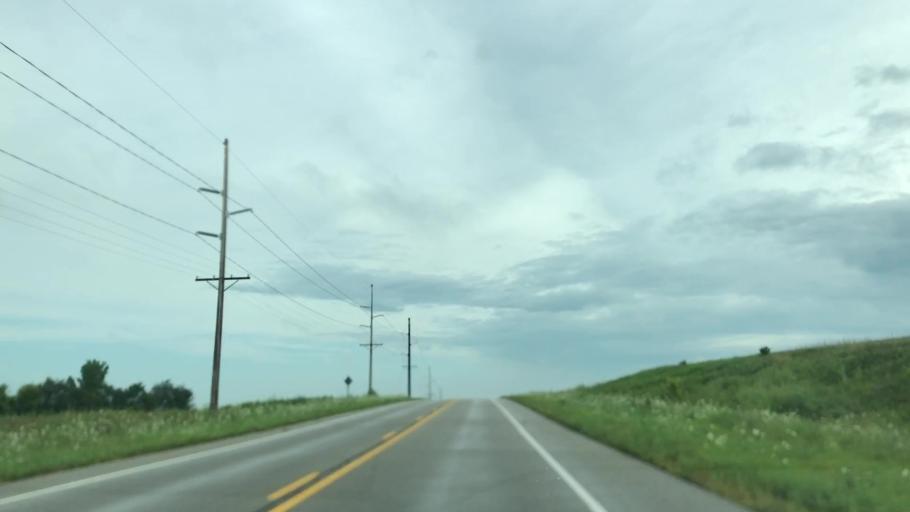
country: US
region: Iowa
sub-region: Marshall County
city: Marshalltown
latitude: 42.0110
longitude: -92.9602
